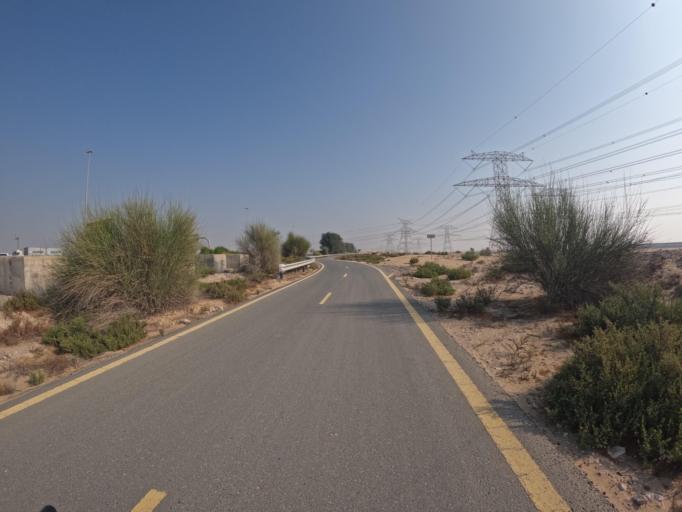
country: AE
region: Dubai
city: Dubai
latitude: 25.0311
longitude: 55.2913
